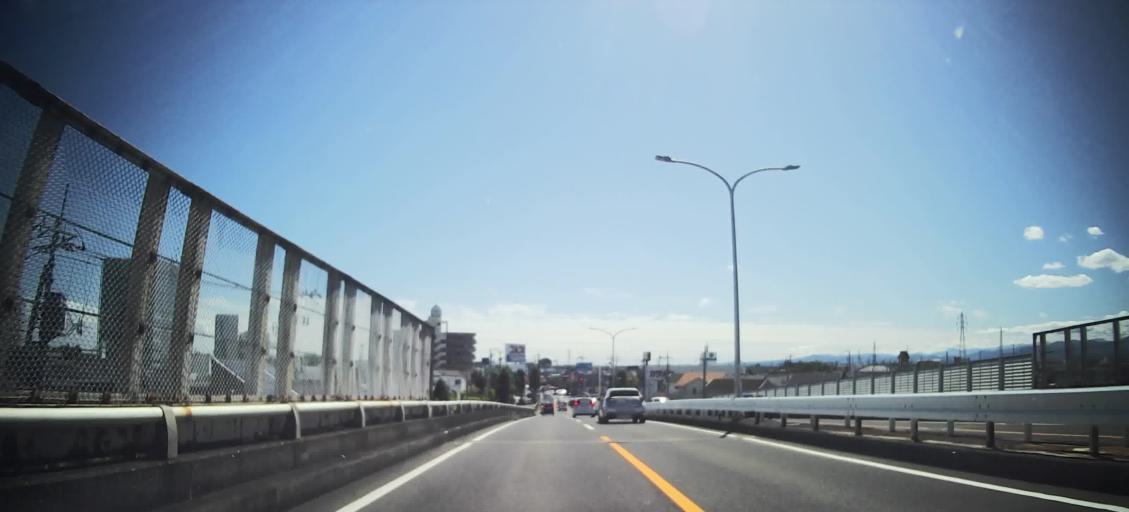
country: JP
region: Gunma
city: Maebashi-shi
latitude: 36.3762
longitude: 139.0424
